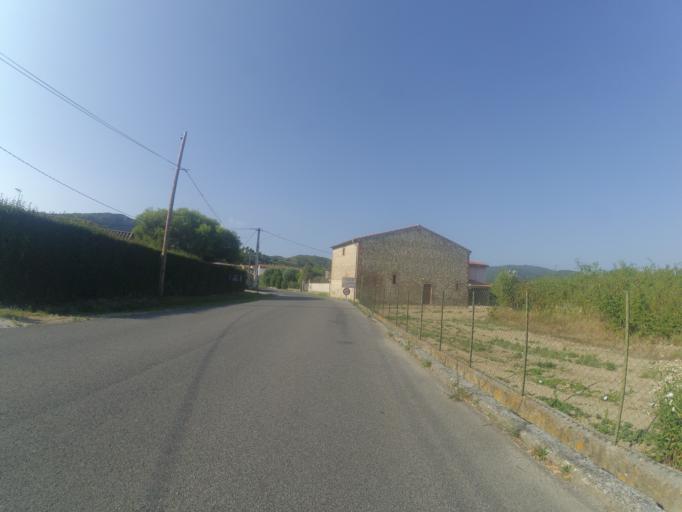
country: FR
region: Languedoc-Roussillon
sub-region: Departement des Pyrenees-Orientales
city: Millas
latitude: 42.6606
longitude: 2.6768
